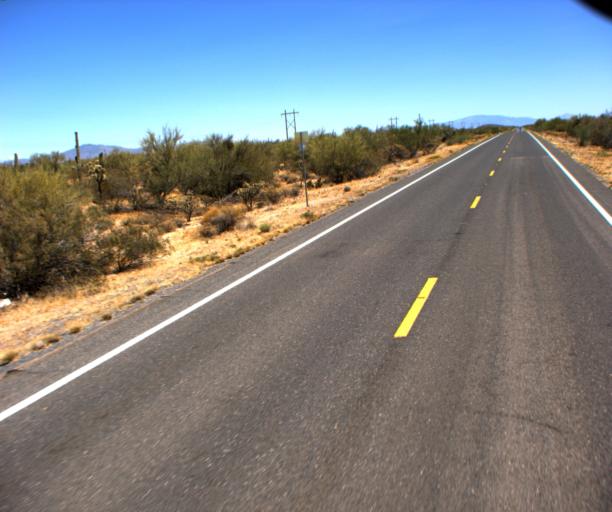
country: US
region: Arizona
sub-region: Pinal County
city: Florence
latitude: 32.8211
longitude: -111.2026
